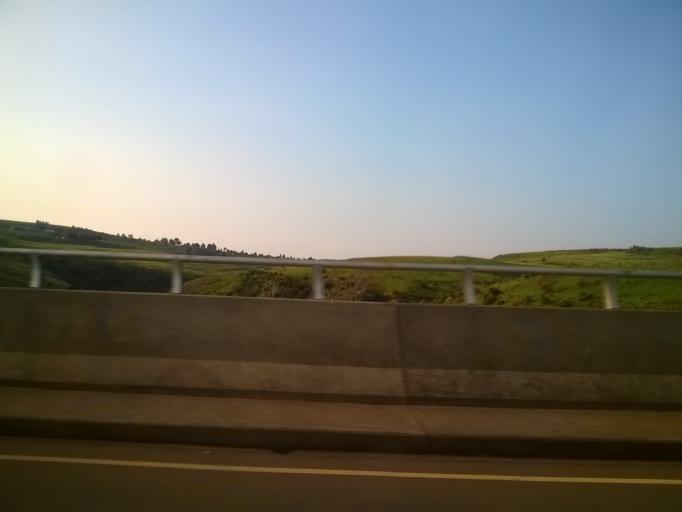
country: LS
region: Leribe
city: Leribe
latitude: -29.0372
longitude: 28.2497
